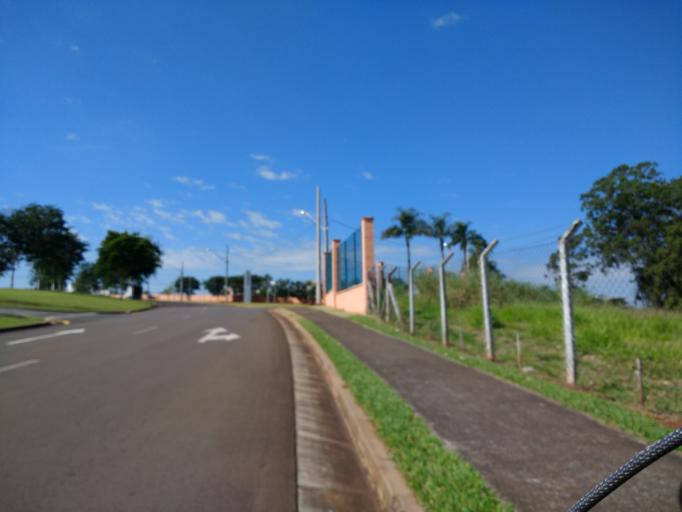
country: BR
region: Parana
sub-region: Londrina
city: Londrina
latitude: -23.3528
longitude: -51.1890
